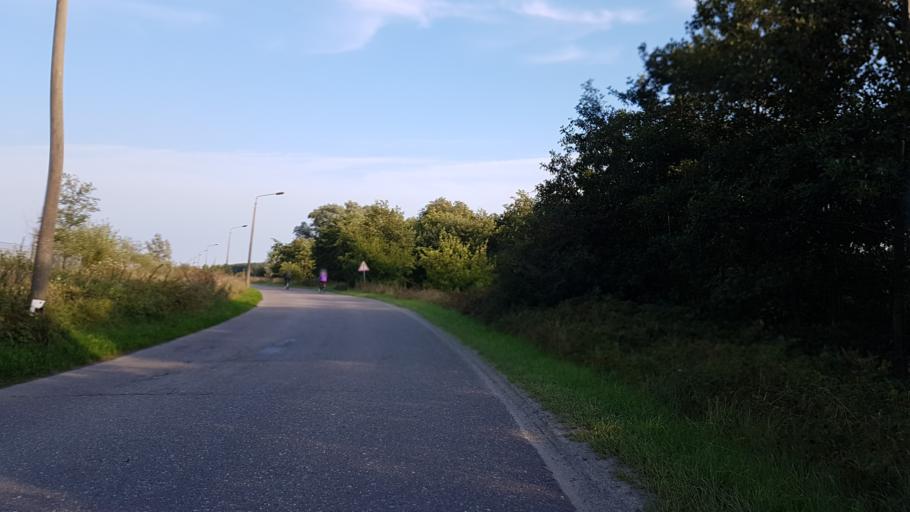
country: DE
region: Mecklenburg-Vorpommern
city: Sagard
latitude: 54.4951
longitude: 13.5532
